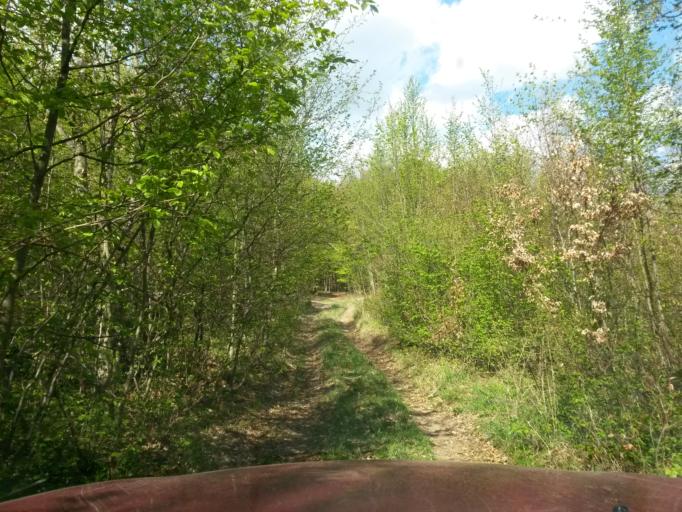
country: SK
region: Presovsky
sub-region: Okres Presov
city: Presov
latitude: 48.9491
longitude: 21.1363
